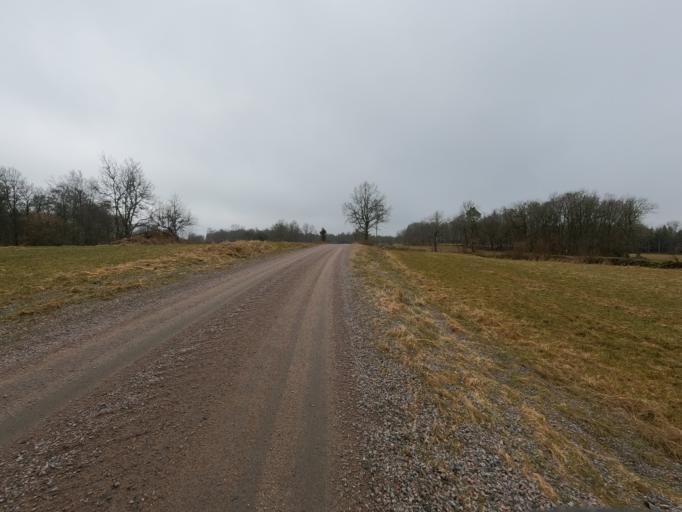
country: SE
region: Kronoberg
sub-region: Markaryds Kommun
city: Stromsnasbruk
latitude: 56.8251
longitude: 13.5642
